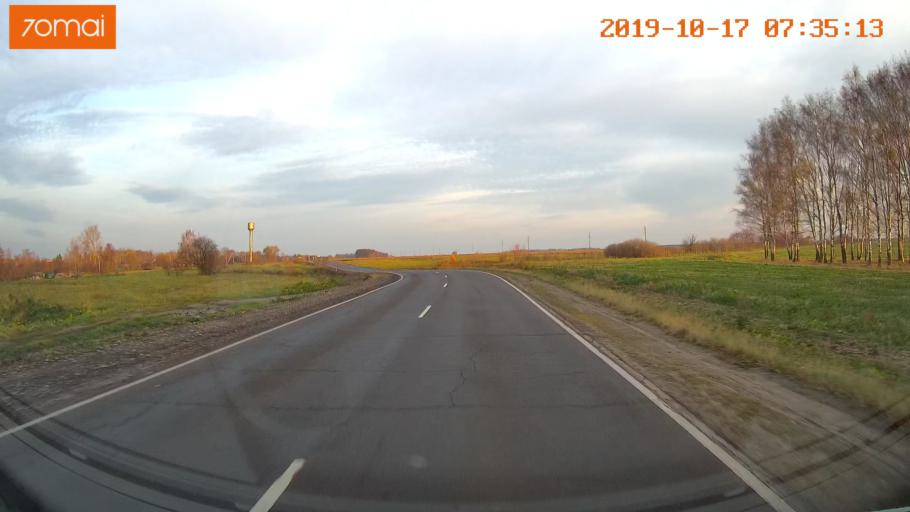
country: RU
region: Ivanovo
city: Gavrilov Posad
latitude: 56.4258
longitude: 39.9317
